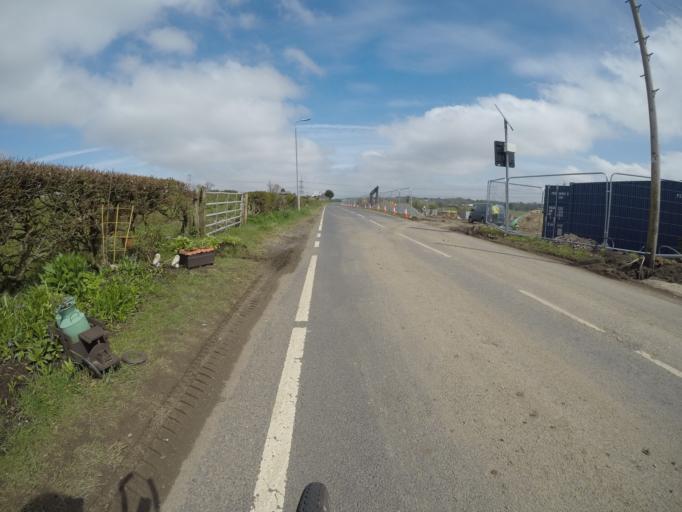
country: GB
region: Scotland
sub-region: East Ayrshire
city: Stewarton
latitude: 55.7024
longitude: -4.4763
